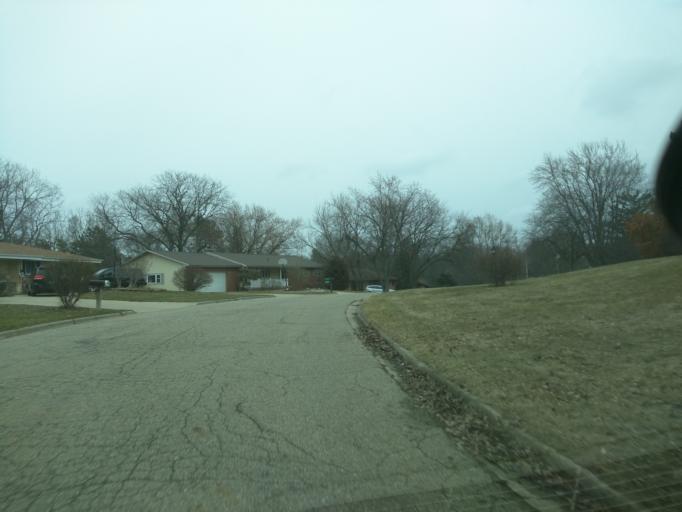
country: US
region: Michigan
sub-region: Eaton County
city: Waverly
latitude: 42.7573
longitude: -84.6150
